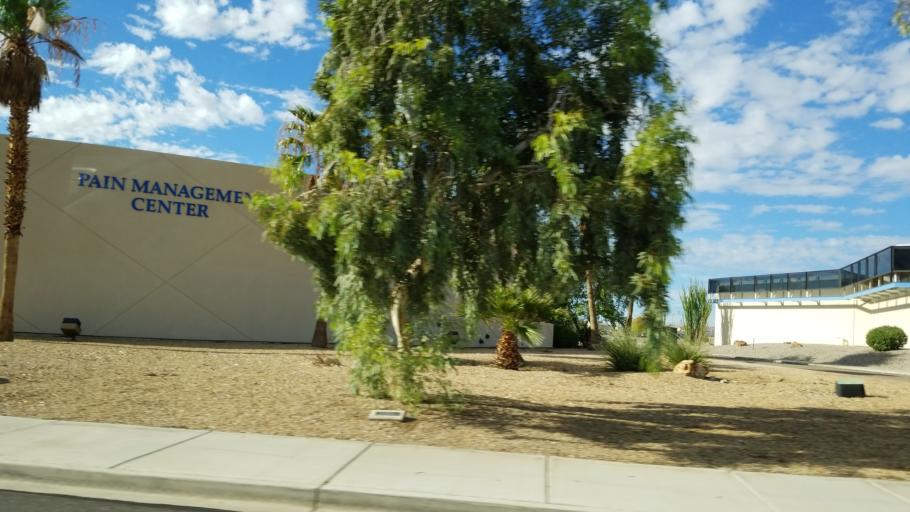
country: US
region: Arizona
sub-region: Mohave County
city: Lake Havasu City
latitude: 34.4775
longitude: -114.3389
